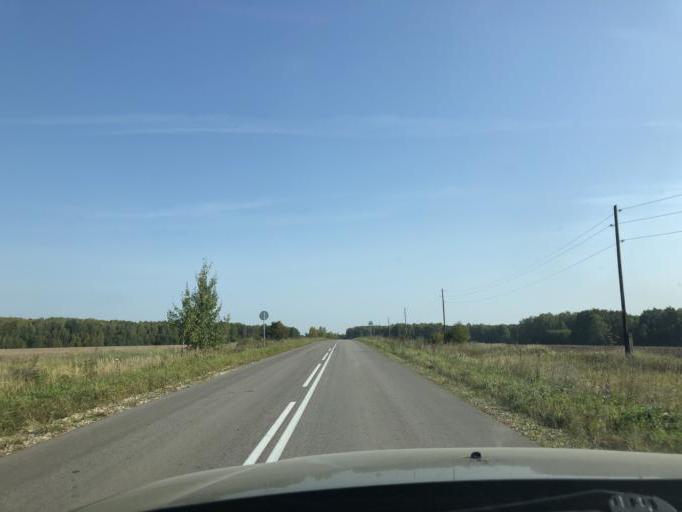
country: RU
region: Tula
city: Novogurovskiy
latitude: 54.4295
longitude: 37.3320
